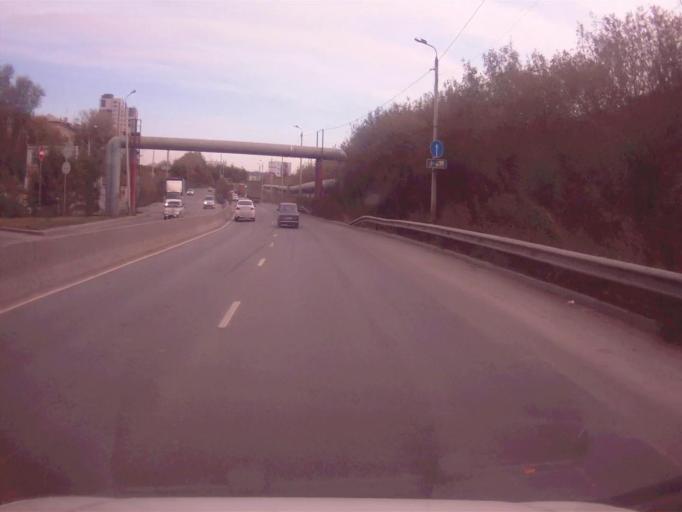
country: RU
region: Chelyabinsk
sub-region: Gorod Chelyabinsk
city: Chelyabinsk
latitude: 55.1591
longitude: 61.4325
